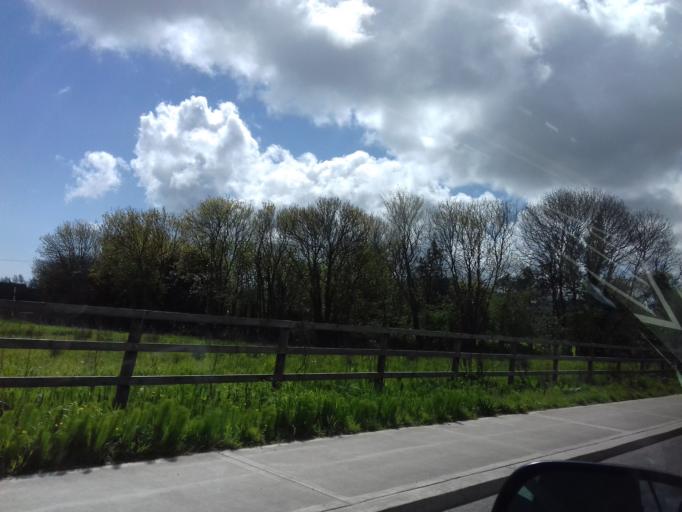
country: IE
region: Leinster
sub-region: Loch Garman
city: Loch Garman
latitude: 52.3580
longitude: -6.4528
